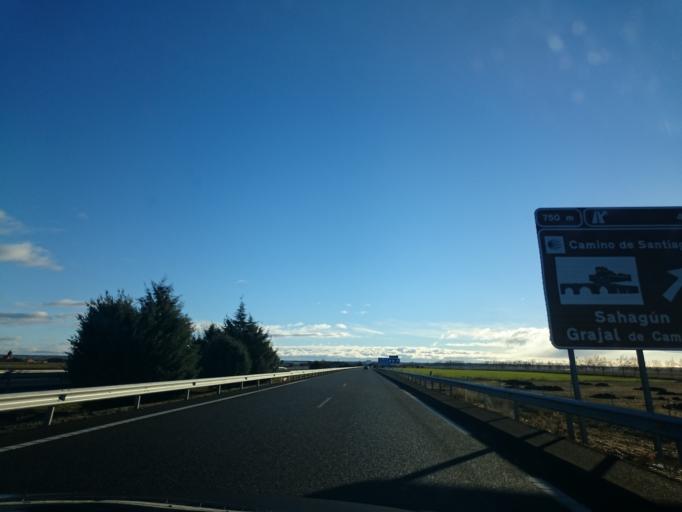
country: ES
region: Castille and Leon
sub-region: Provincia de Leon
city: Calzada del Coto
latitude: 42.3856
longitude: -5.0916
